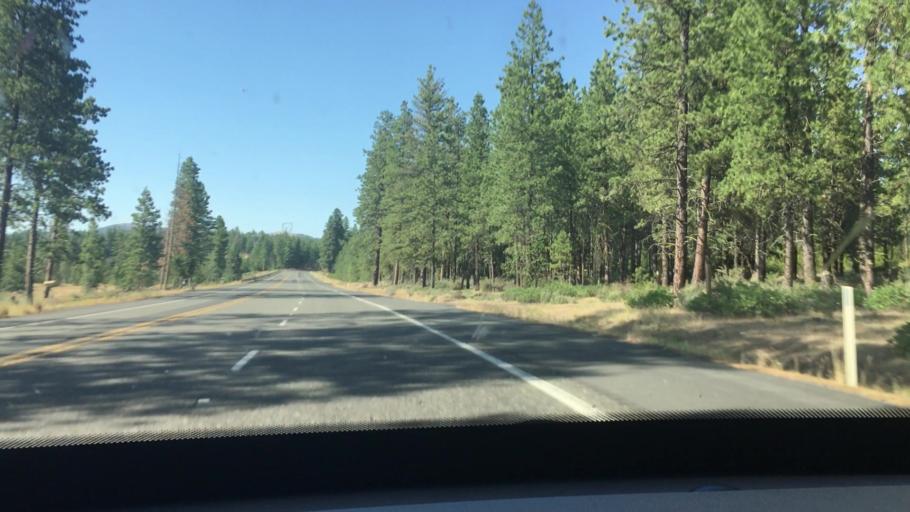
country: US
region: Washington
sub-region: Klickitat County
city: Goldendale
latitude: 45.9259
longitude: -120.6985
